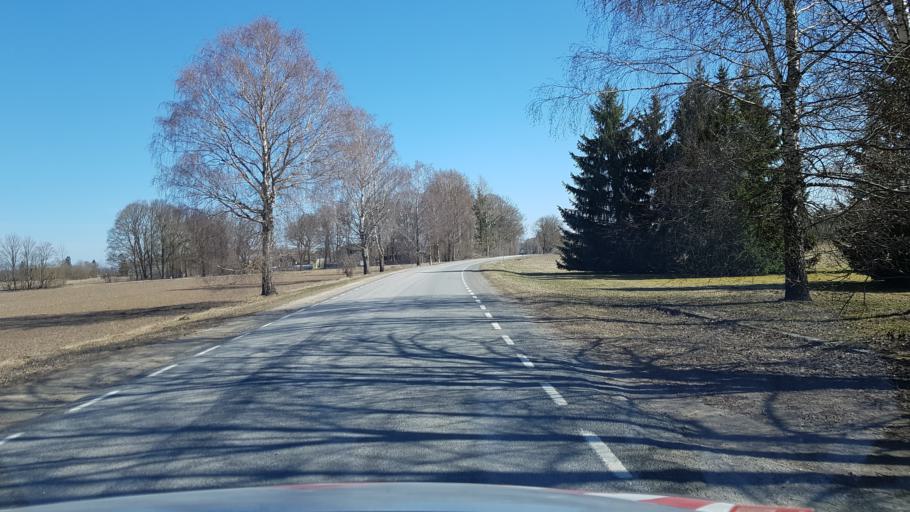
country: EE
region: Laeaene-Virumaa
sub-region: Vaeike-Maarja vald
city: Vaike-Maarja
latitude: 59.1294
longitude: 26.2601
